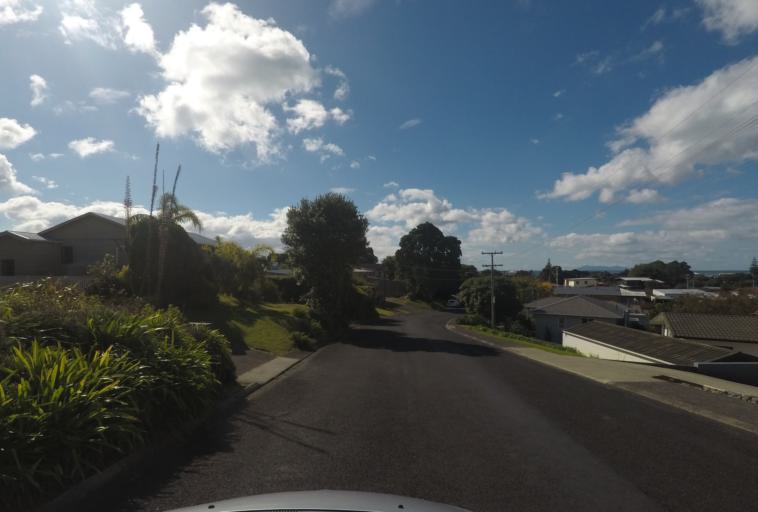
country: NZ
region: Bay of Plenty
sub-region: Western Bay of Plenty District
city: Waihi Beach
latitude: -37.4117
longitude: 175.9390
